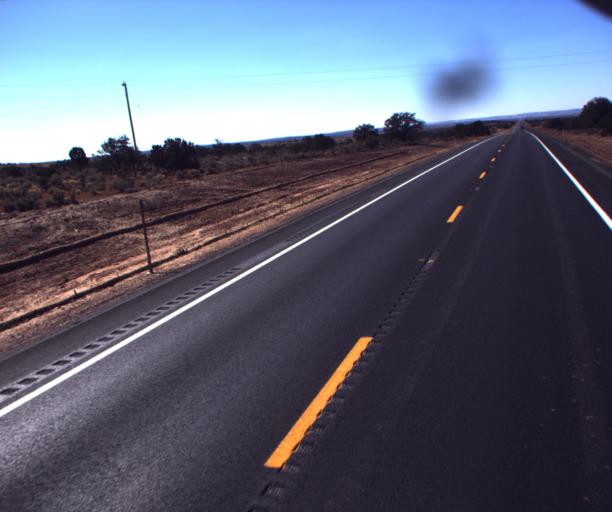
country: US
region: Arizona
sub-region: Apache County
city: Ganado
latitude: 35.7183
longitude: -109.3912
